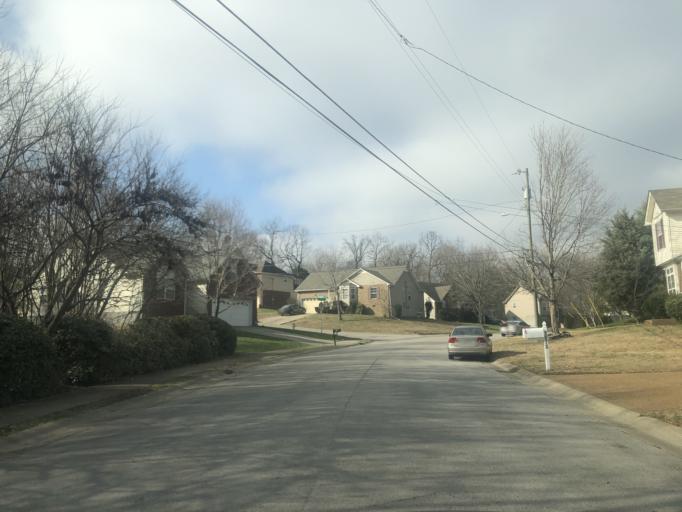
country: US
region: Tennessee
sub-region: Rutherford County
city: La Vergne
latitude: 36.0844
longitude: -86.6604
